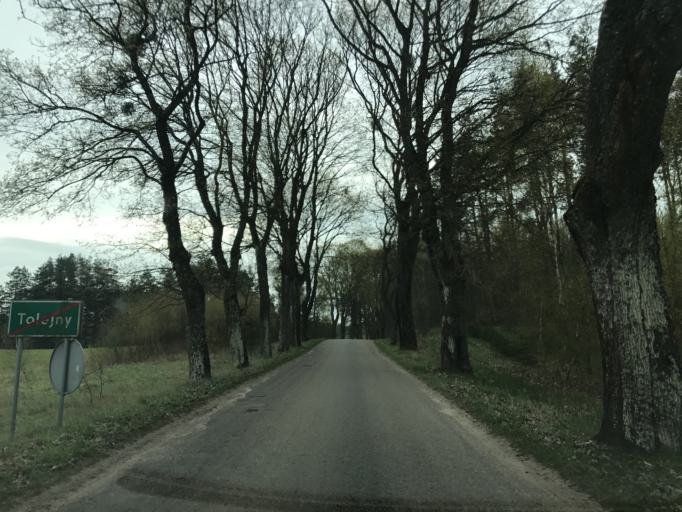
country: PL
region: Warmian-Masurian Voivodeship
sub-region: Powiat olsztynski
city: Olsztynek
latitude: 53.6149
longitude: 20.2494
